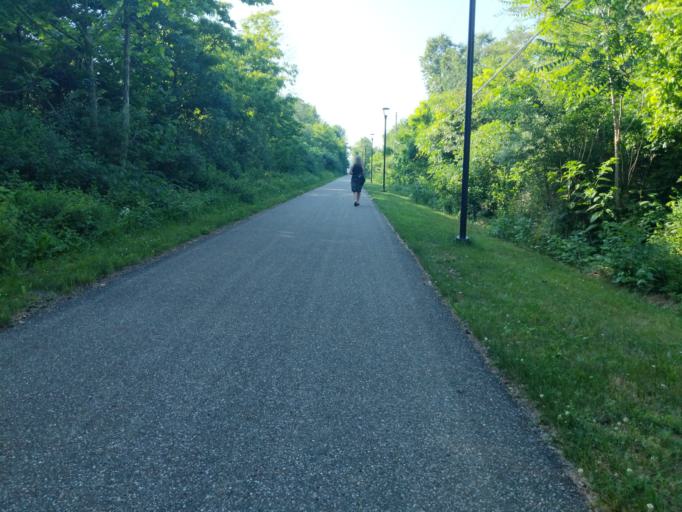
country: US
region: Ohio
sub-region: Athens County
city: Nelsonville
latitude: 39.4367
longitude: -82.2165
